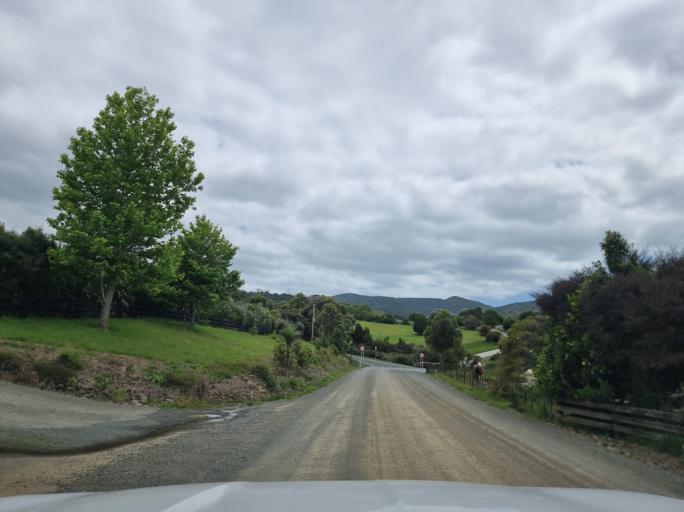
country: NZ
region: Auckland
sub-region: Auckland
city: Wellsford
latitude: -36.0910
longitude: 174.5299
